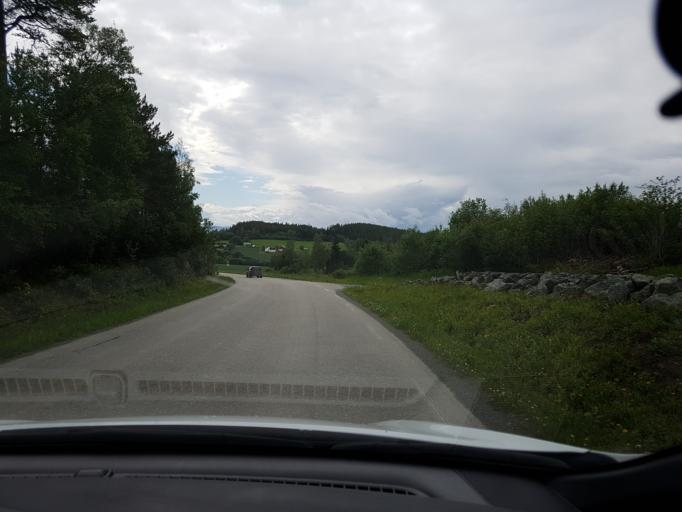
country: NO
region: Nord-Trondelag
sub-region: Frosta
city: Frosta
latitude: 63.6029
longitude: 10.7338
